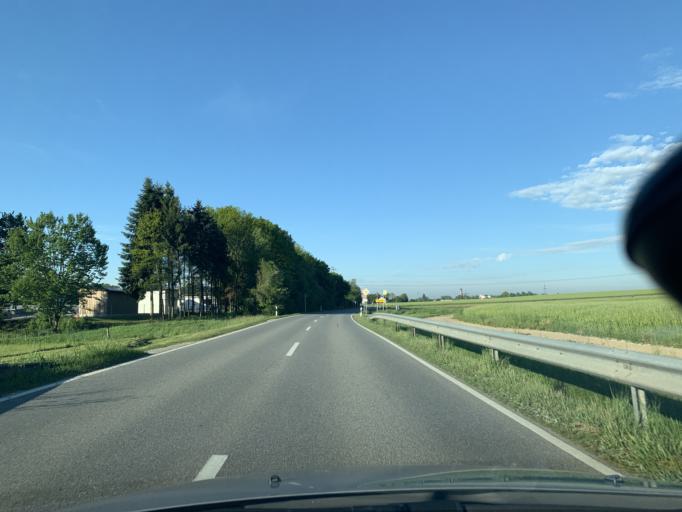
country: DE
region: Bavaria
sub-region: Lower Bavaria
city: Vilsbiburg
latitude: 48.4656
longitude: 12.3761
